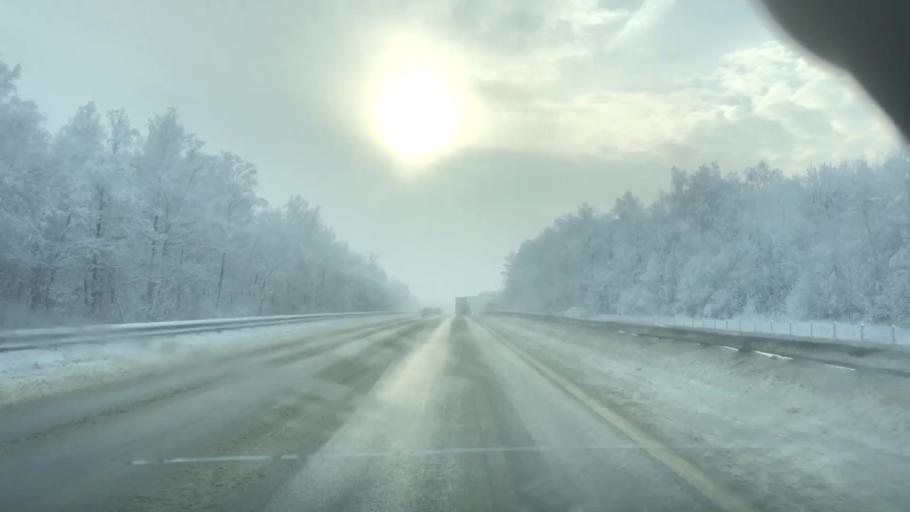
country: RU
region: Tula
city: Venev
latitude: 54.5249
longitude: 38.1681
